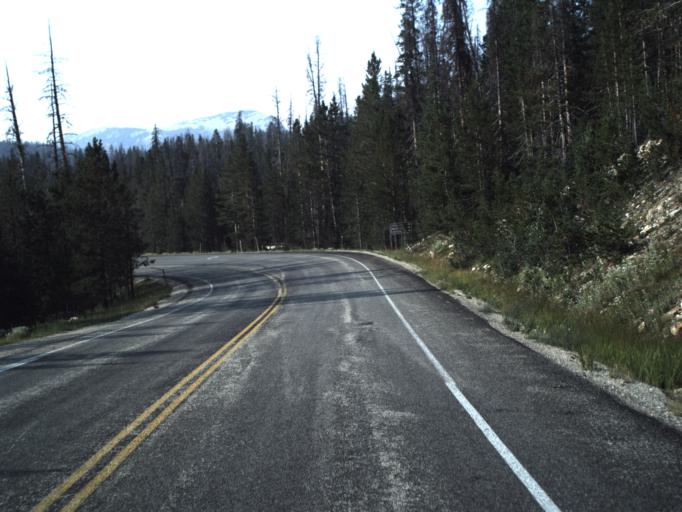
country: US
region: Utah
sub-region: Summit County
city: Kamas
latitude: 40.6764
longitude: -110.9512
